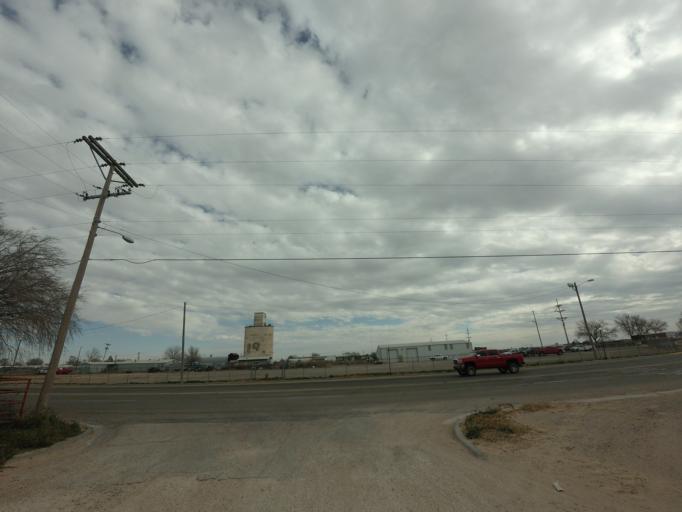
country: US
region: New Mexico
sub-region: Curry County
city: Clovis
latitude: 34.3908
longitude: -103.2207
